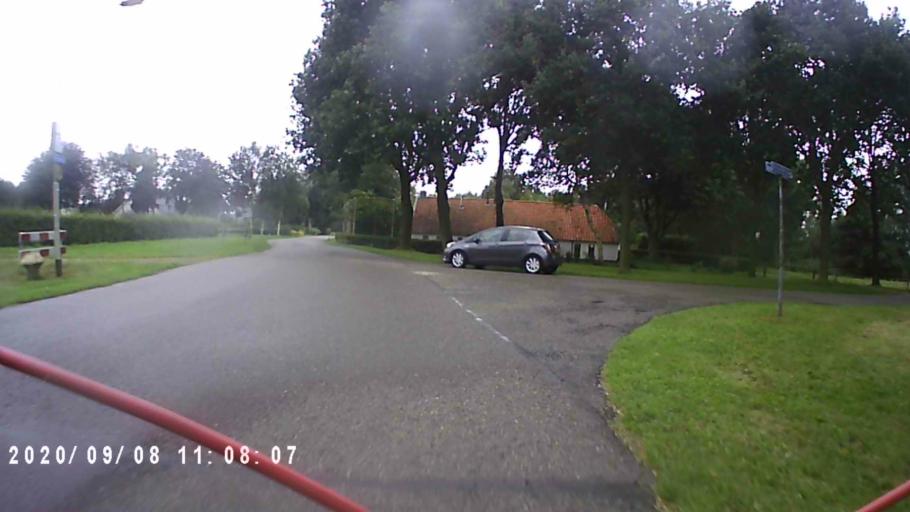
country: NL
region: Groningen
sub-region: Gemeente Hoogezand-Sappemeer
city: Hoogezand
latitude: 53.1865
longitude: 6.7006
